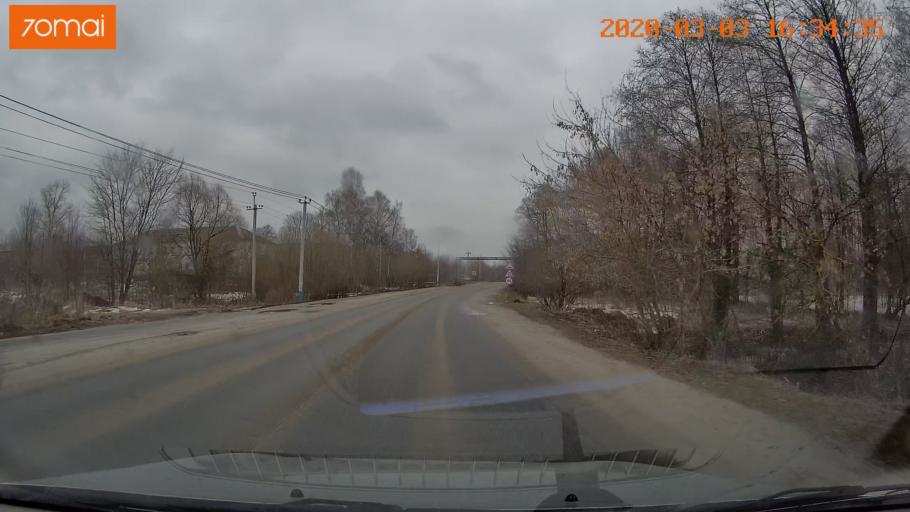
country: RU
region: Moskovskaya
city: Lopatinskiy
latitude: 55.4073
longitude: 38.7589
